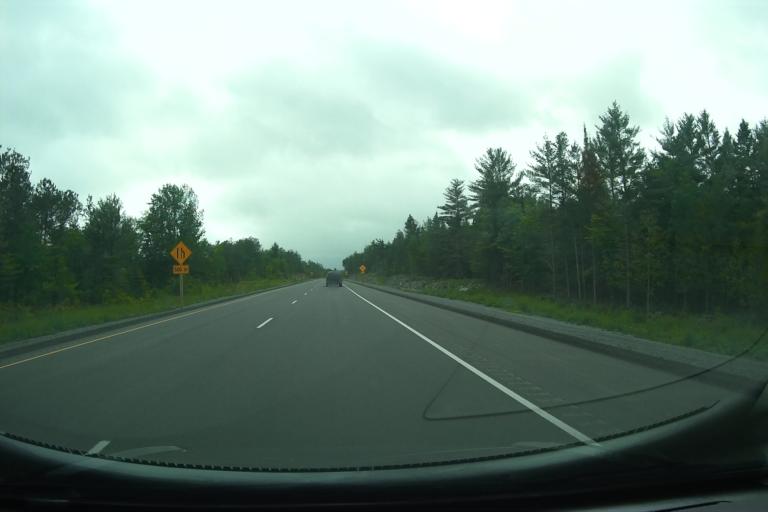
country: CA
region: Ontario
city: Arnprior
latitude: 45.4374
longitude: -76.4425
